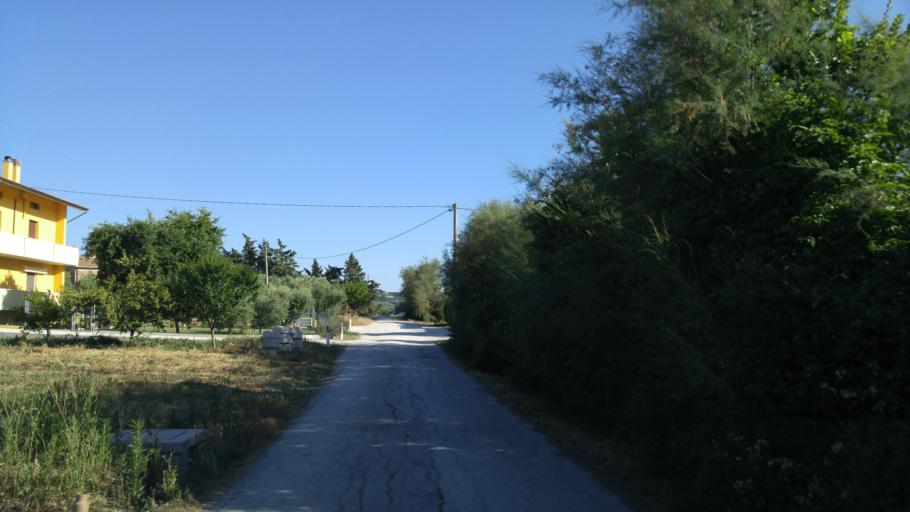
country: IT
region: The Marches
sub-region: Provincia di Pesaro e Urbino
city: Cartoceto
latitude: 43.7914
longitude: 12.8867
